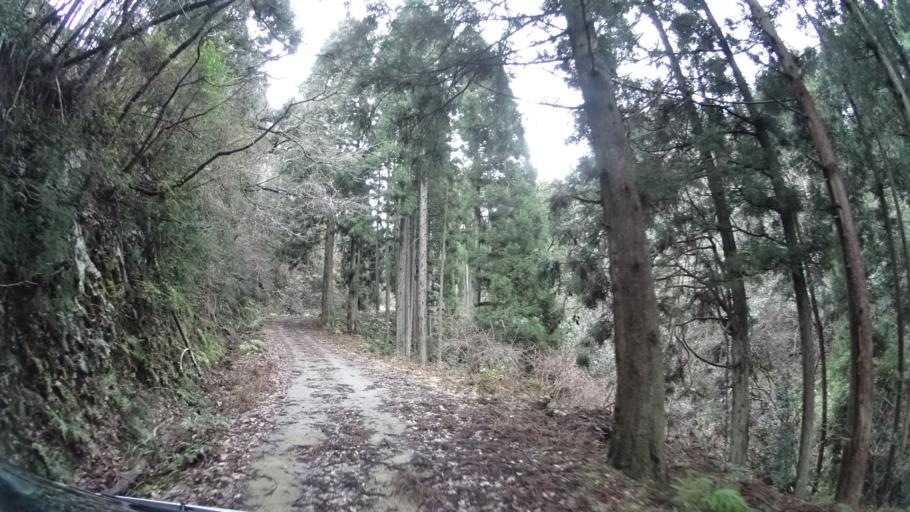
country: JP
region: Kyoto
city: Ayabe
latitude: 35.3127
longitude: 135.3729
